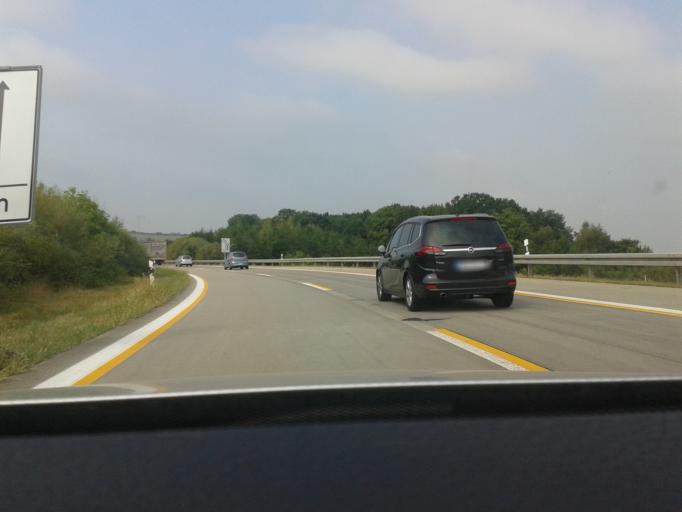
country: DE
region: Saxony
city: Wilsdruff
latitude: 51.0638
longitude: 13.6021
